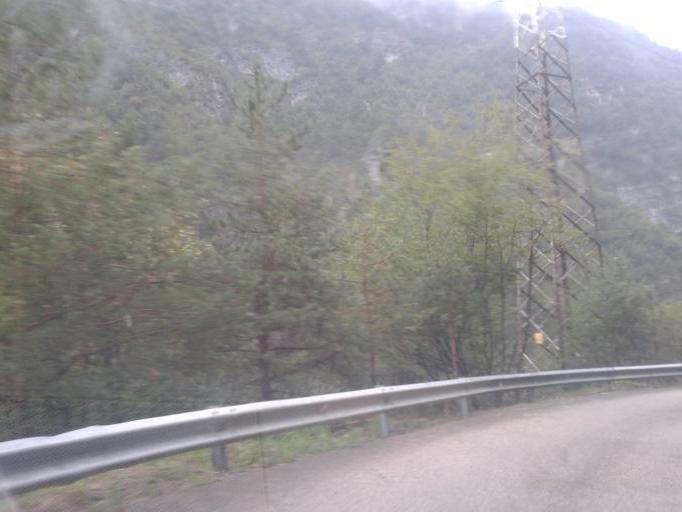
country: IT
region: Trentino-Alto Adige
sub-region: Provincia di Trento
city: Storo
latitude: 45.8432
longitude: 10.6136
